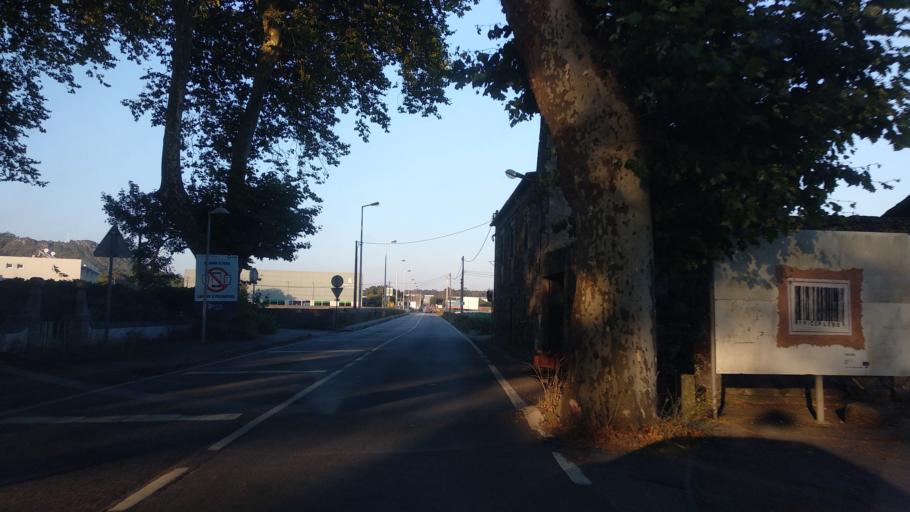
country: PT
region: Braga
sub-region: Esposende
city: Esposende
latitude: 41.5315
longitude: -8.7757
